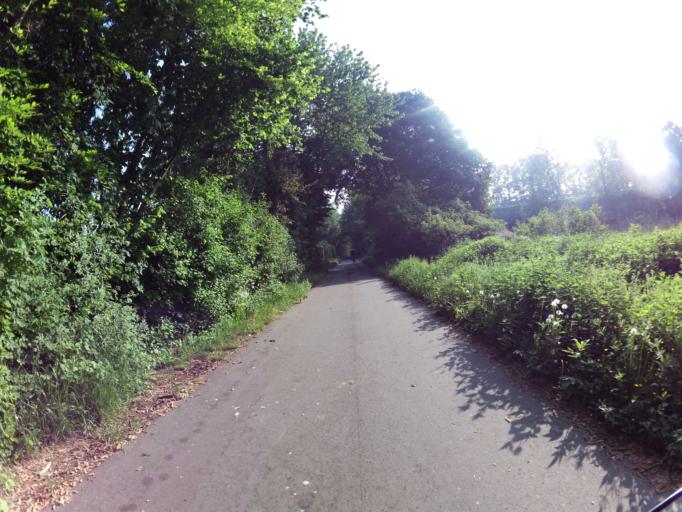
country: DE
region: North Rhine-Westphalia
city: Siersdorf
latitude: 50.8688
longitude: 6.2210
